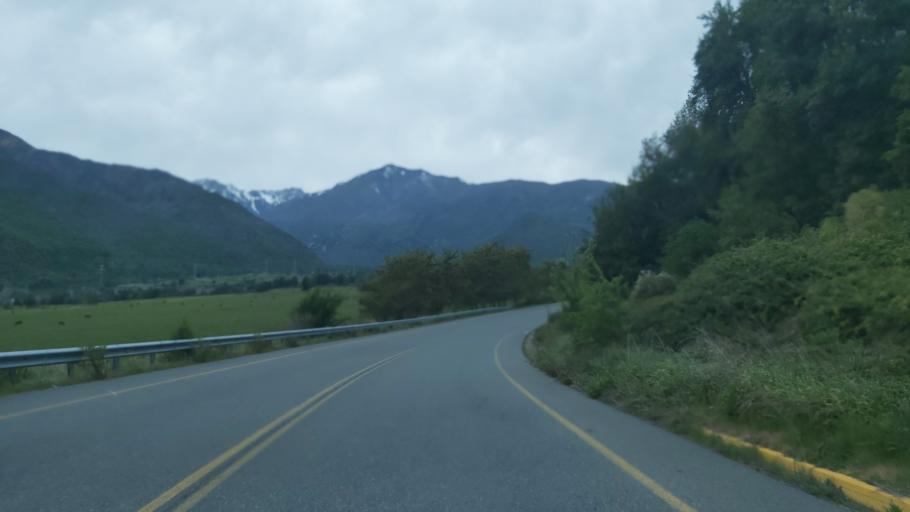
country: CL
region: Maule
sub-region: Provincia de Linares
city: Colbun
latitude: -35.8121
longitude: -70.8690
